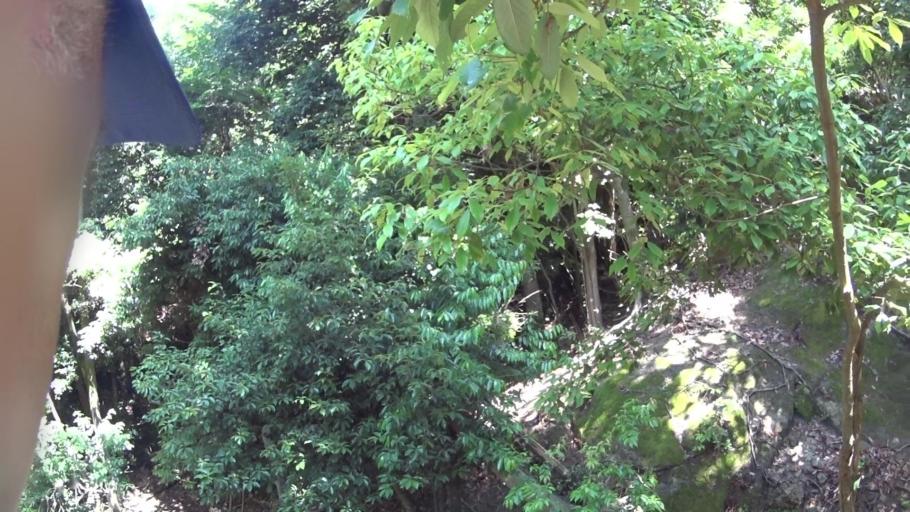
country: JP
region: Kyoto
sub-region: Kyoto-shi
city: Kamigyo-ku
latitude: 35.0394
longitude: 135.8012
